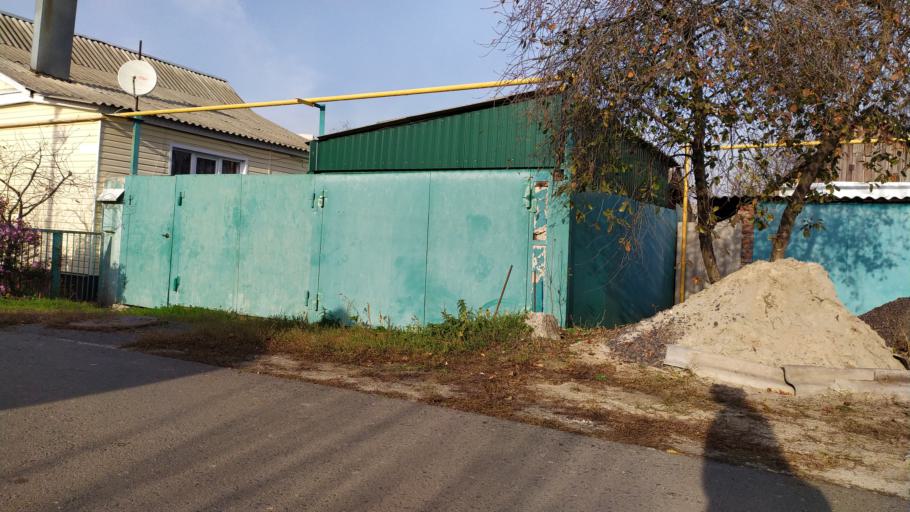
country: RU
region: Kursk
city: Kursk
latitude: 51.6458
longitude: 36.1448
